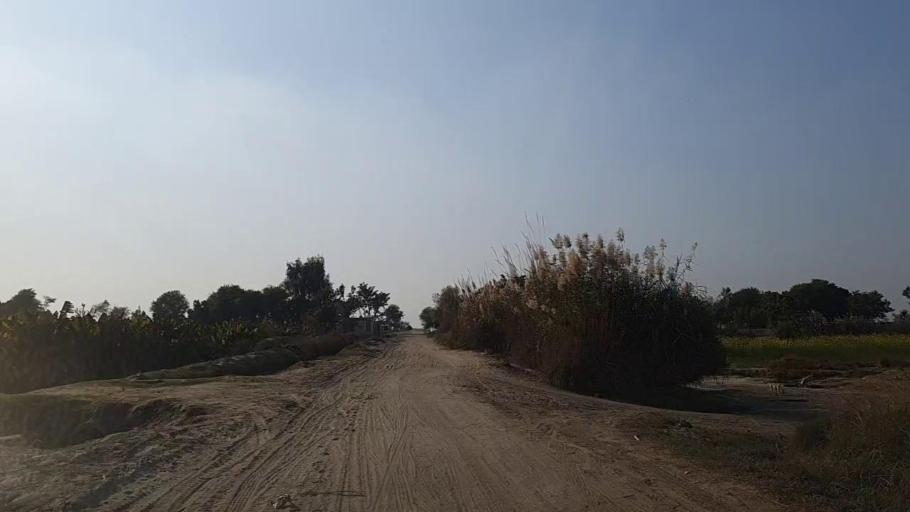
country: PK
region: Sindh
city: Daur
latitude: 26.4043
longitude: 68.2610
